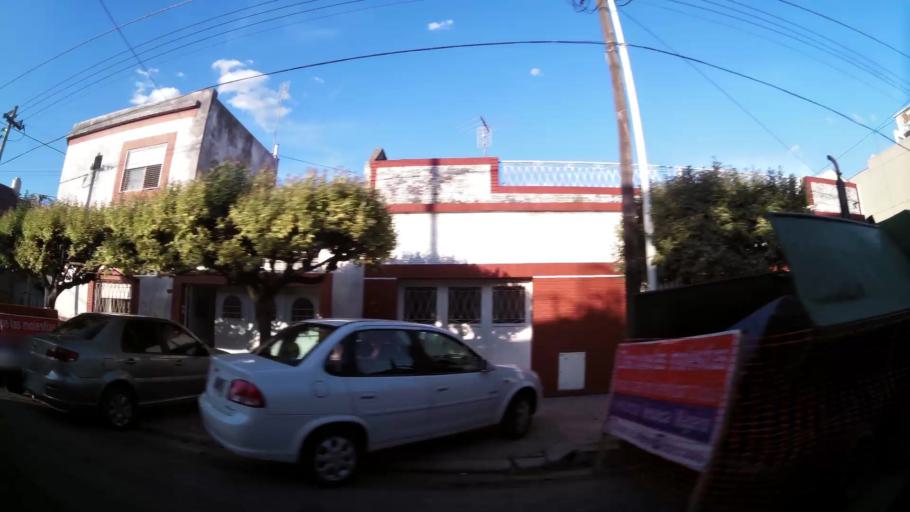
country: AR
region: Buenos Aires F.D.
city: Villa Lugano
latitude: -34.6926
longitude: -58.4849
